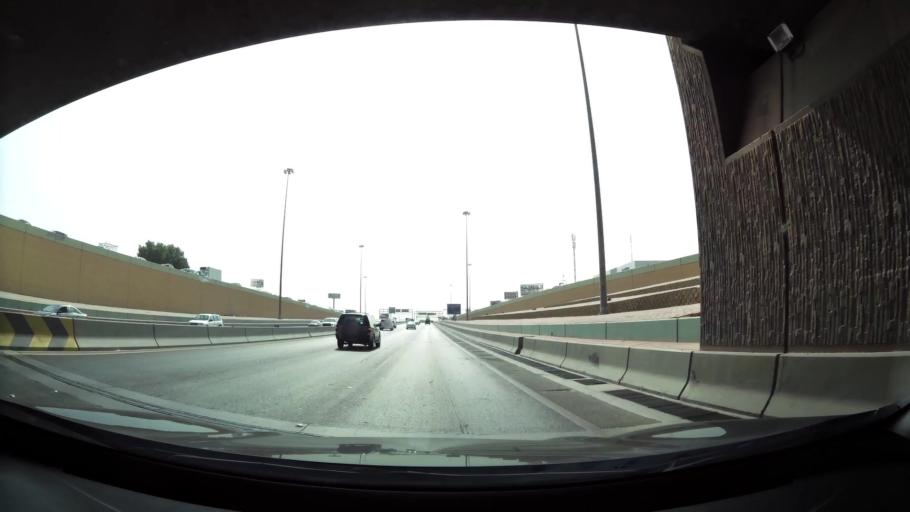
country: KW
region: Al Asimah
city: Ar Rabiyah
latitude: 29.3142
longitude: 47.9421
